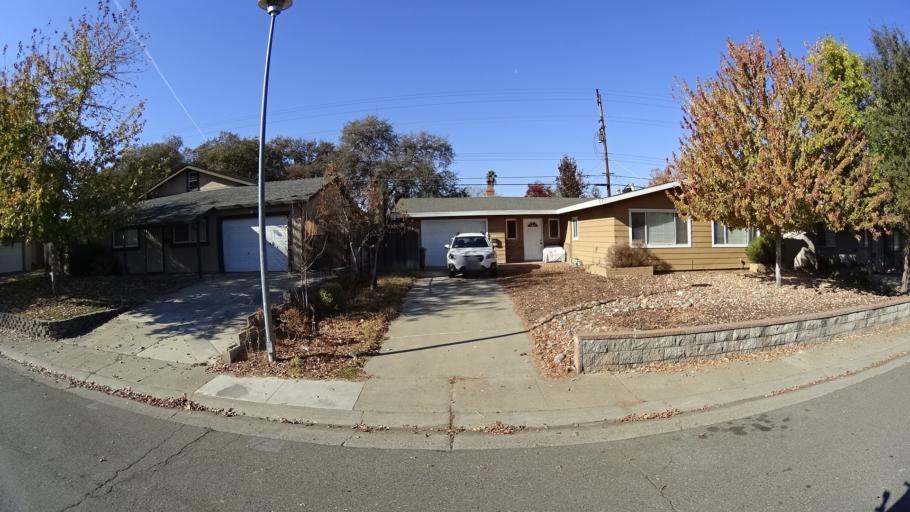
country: US
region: California
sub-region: Sacramento County
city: Antelope
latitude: 38.7126
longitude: -121.3084
